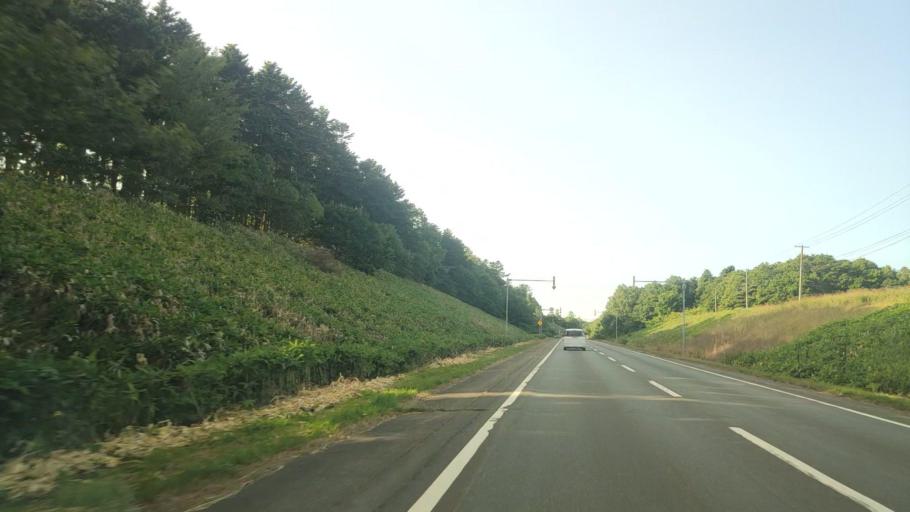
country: JP
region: Hokkaido
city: Makubetsu
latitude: 45.0637
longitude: 141.7482
